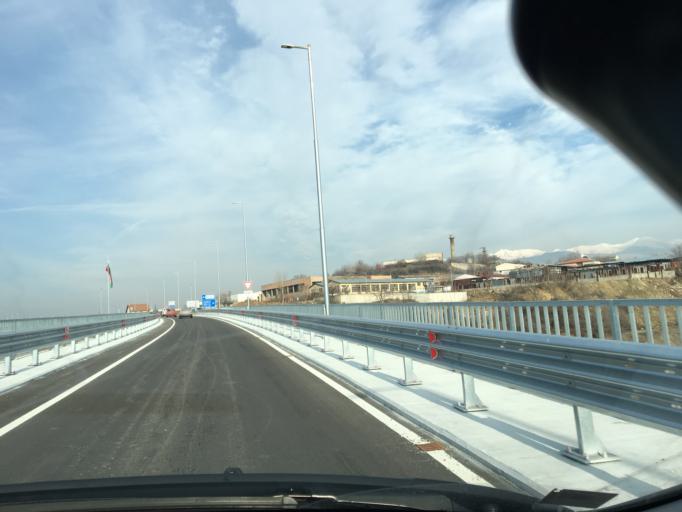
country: BG
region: Blagoevgrad
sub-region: Obshtina Sandanski
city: Sandanski
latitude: 41.5400
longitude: 23.2577
